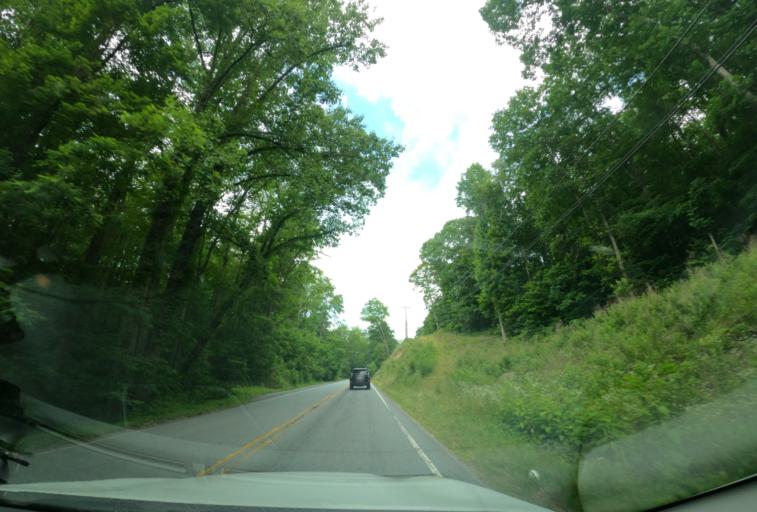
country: US
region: North Carolina
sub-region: Jackson County
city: Cullowhee
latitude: 35.1080
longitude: -83.1345
